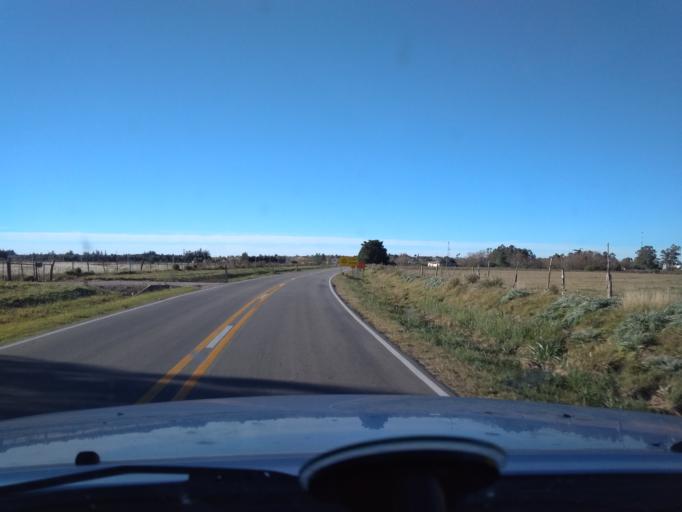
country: UY
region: Canelones
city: Santa Rosa
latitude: -34.5097
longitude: -56.0533
